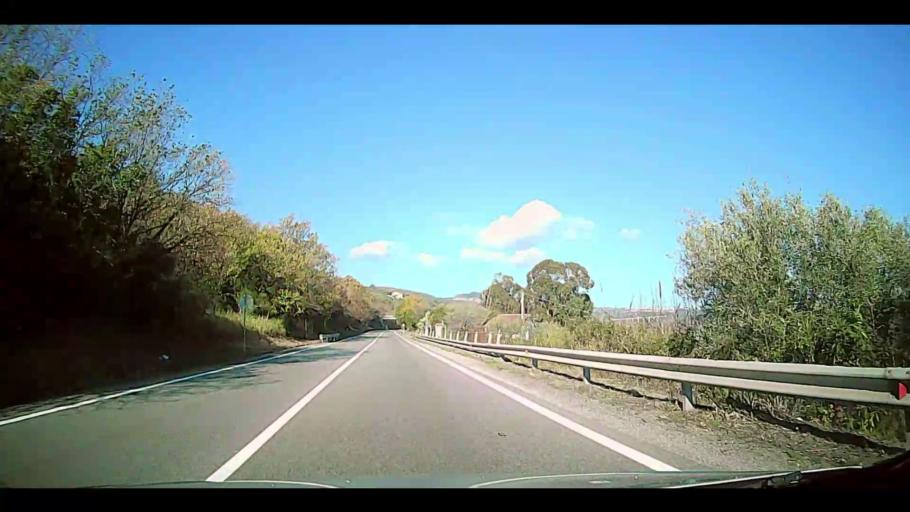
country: IT
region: Calabria
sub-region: Provincia di Crotone
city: Caccuri
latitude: 39.2027
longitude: 16.8094
